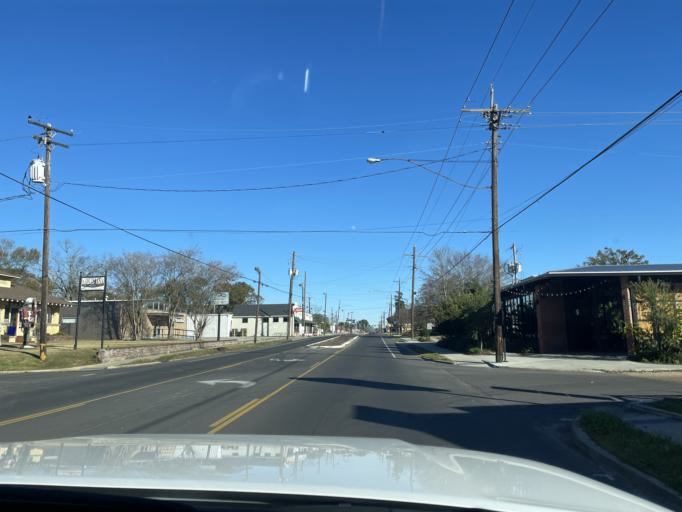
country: US
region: Louisiana
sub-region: East Baton Rouge Parish
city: Baton Rouge
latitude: 30.4442
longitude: -91.1510
